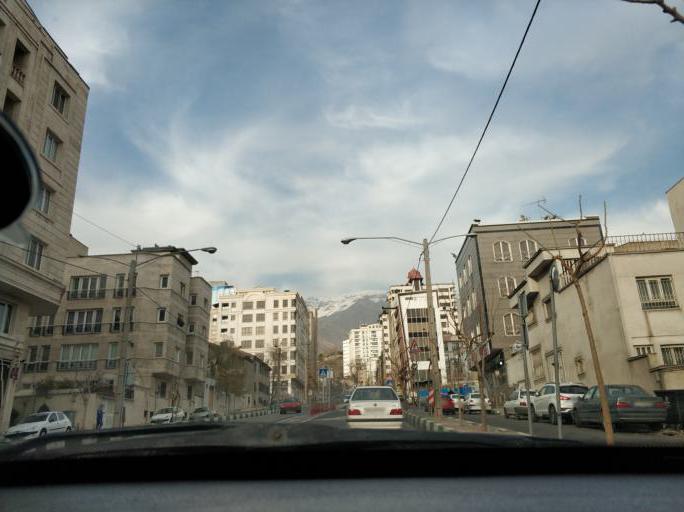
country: IR
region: Tehran
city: Tajrish
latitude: 35.8081
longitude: 51.4836
